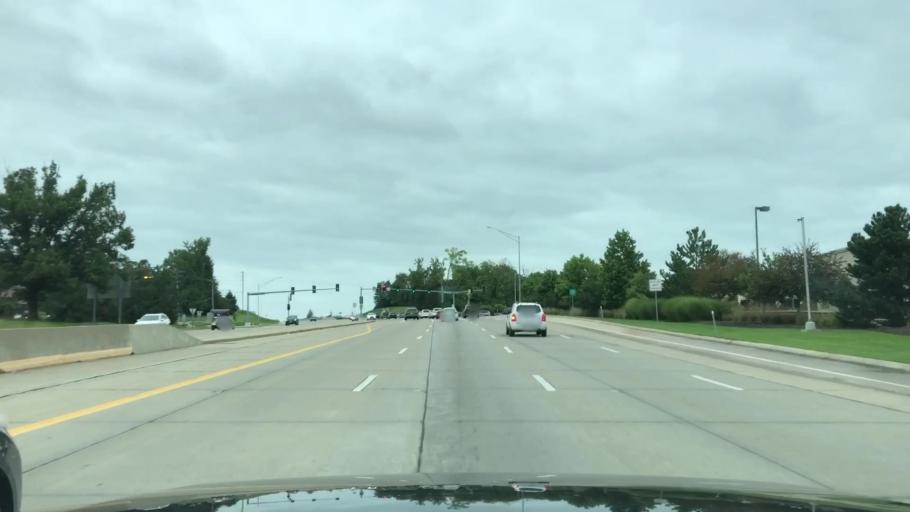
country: US
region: Missouri
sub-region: Saint Louis County
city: Manchester
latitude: 38.5975
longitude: -90.5086
